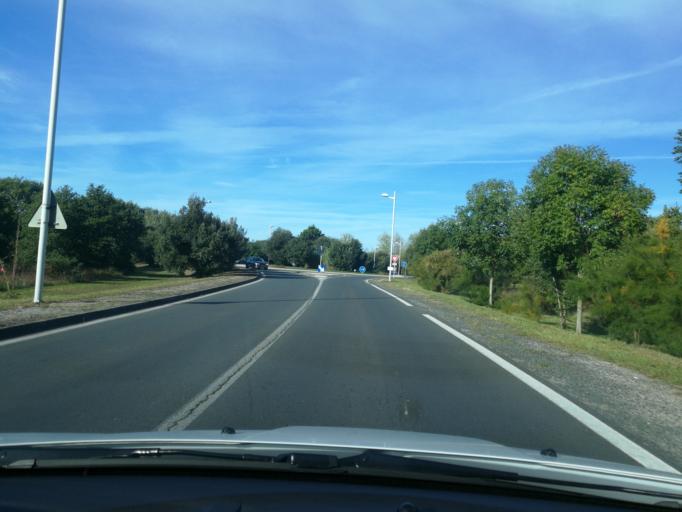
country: FR
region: Poitou-Charentes
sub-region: Departement de la Charente-Maritime
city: Dolus-d'Oleron
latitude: 45.9028
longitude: -1.2515
